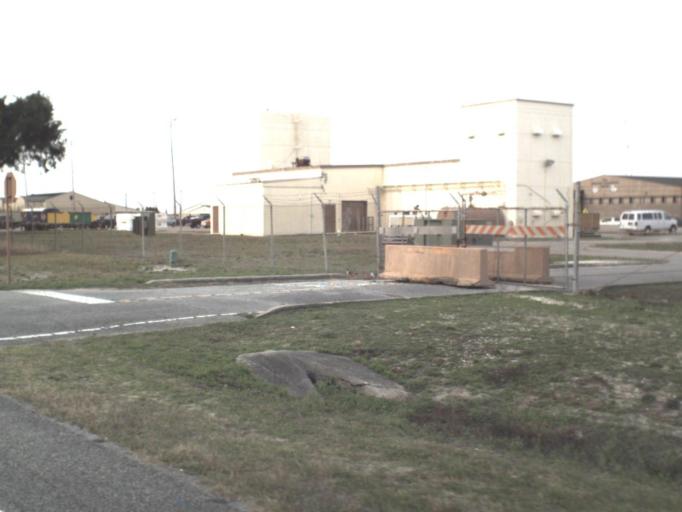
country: US
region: Florida
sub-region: Bay County
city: Tyndall Air Force Base
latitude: 30.0619
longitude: -85.5797
